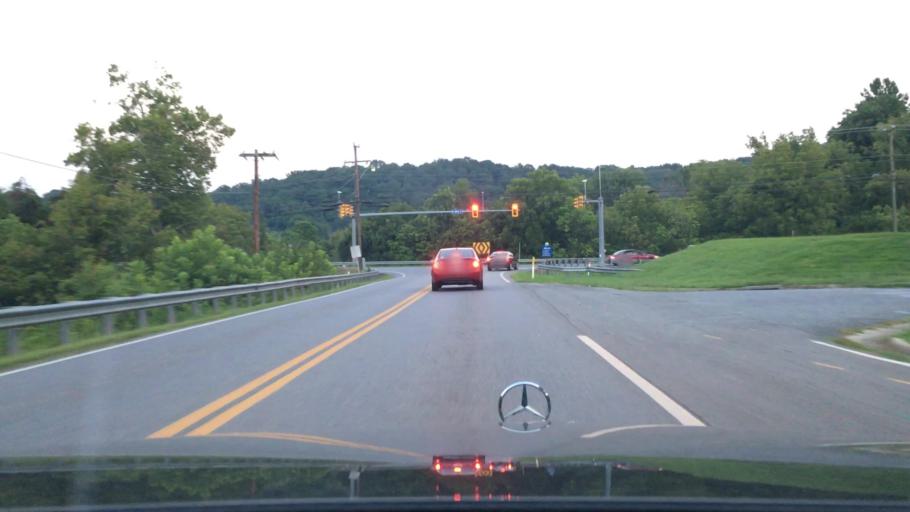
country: US
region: Virginia
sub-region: Campbell County
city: Altavista
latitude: 37.1269
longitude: -79.2717
